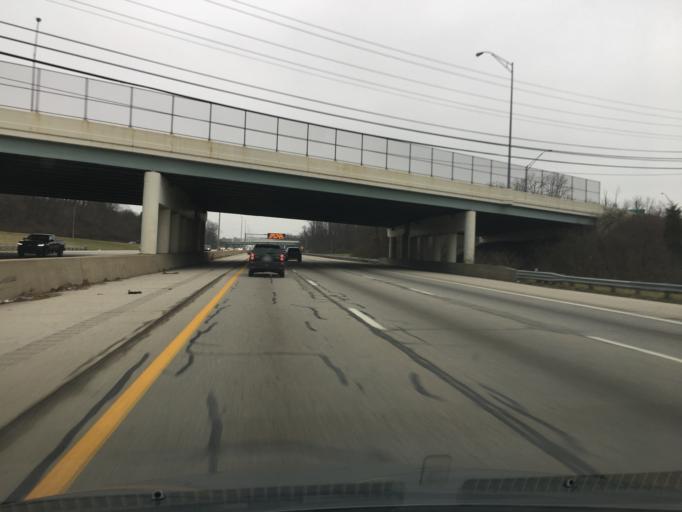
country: US
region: Ohio
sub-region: Hamilton County
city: Highpoint
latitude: 39.2859
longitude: -84.3715
